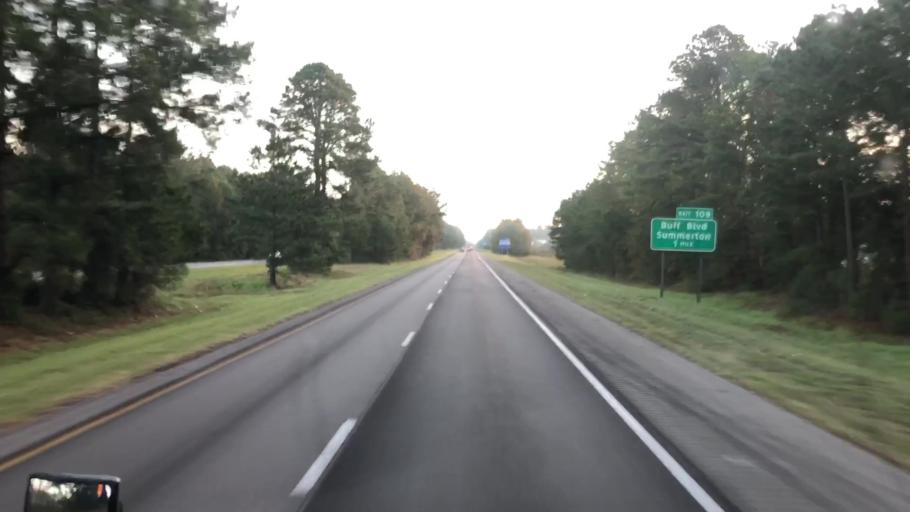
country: US
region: South Carolina
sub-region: Clarendon County
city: Manning
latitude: 33.5773
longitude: -80.3742
